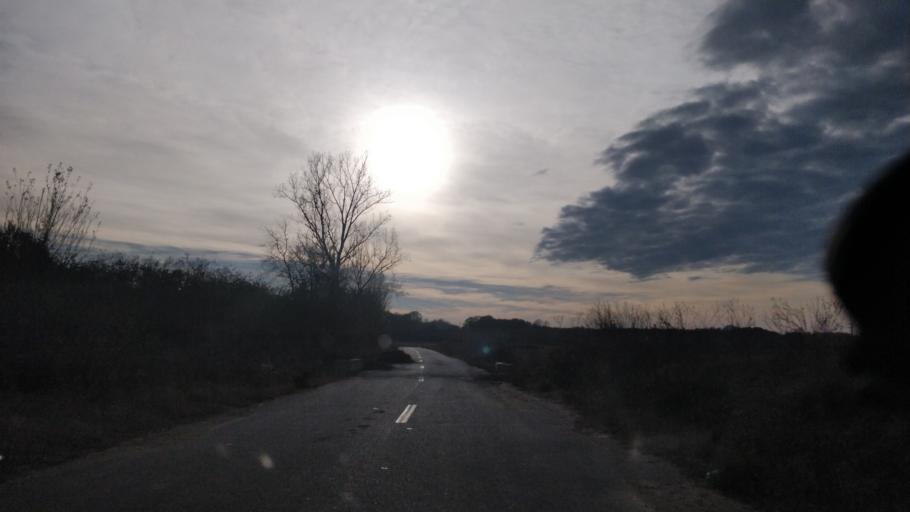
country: RO
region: Giurgiu
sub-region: Comuna Bucsani
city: Bucsani
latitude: 44.3402
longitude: 25.6653
